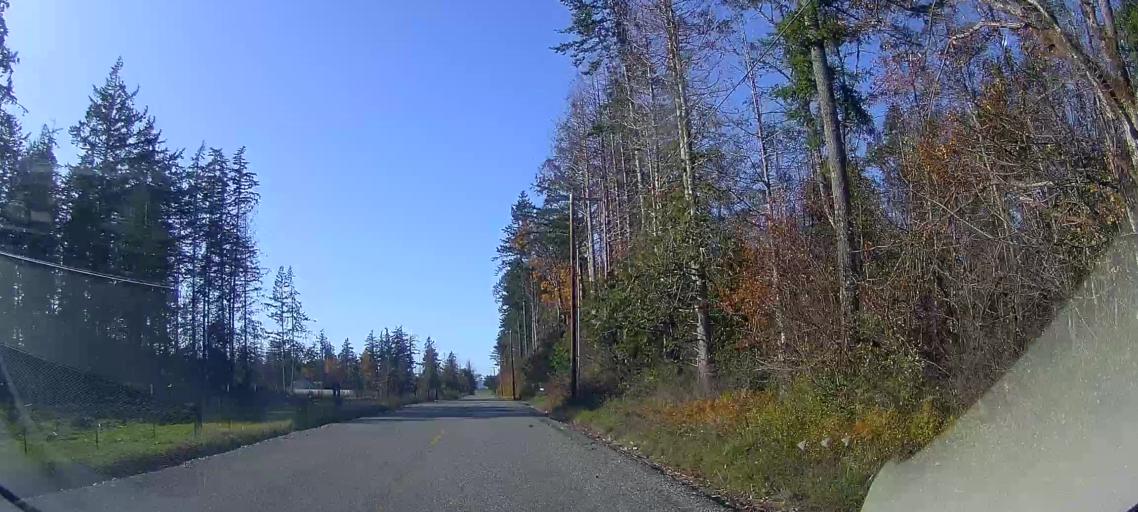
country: US
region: Washington
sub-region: Skagit County
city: Mount Vernon
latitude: 48.3700
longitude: -122.4401
